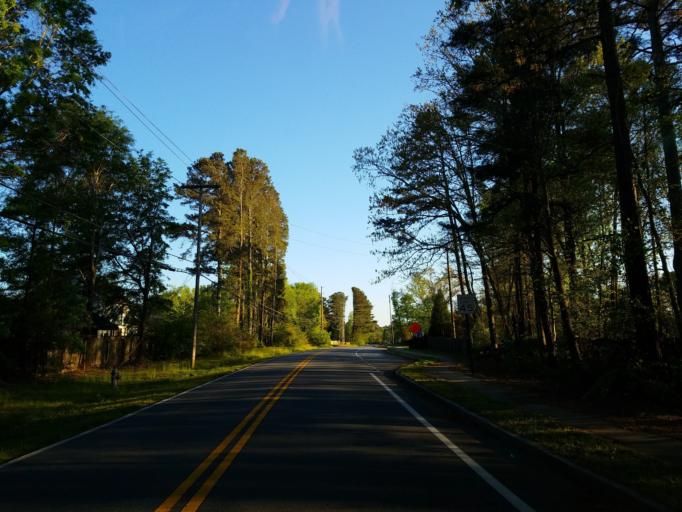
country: US
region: Georgia
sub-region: Cobb County
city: Powder Springs
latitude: 33.9191
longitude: -84.6347
